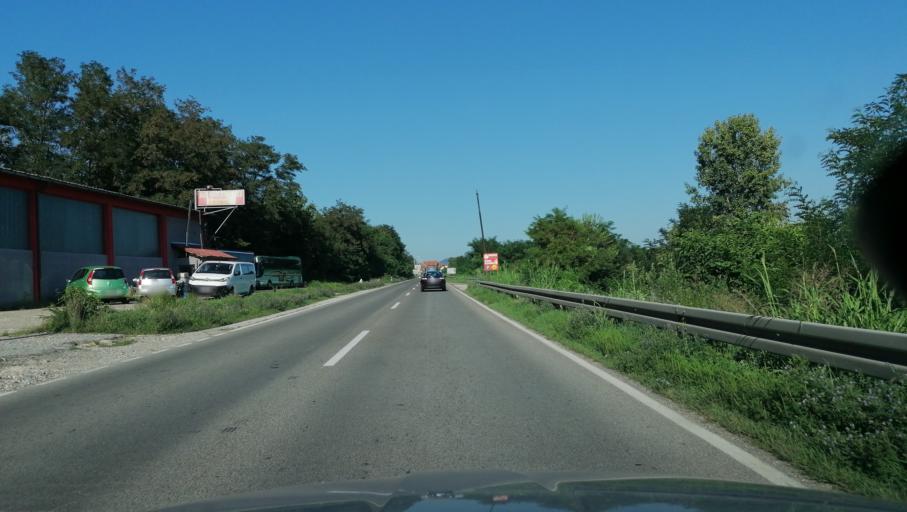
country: RS
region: Central Serbia
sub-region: Raski Okrug
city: Kraljevo
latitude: 43.7187
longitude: 20.6298
